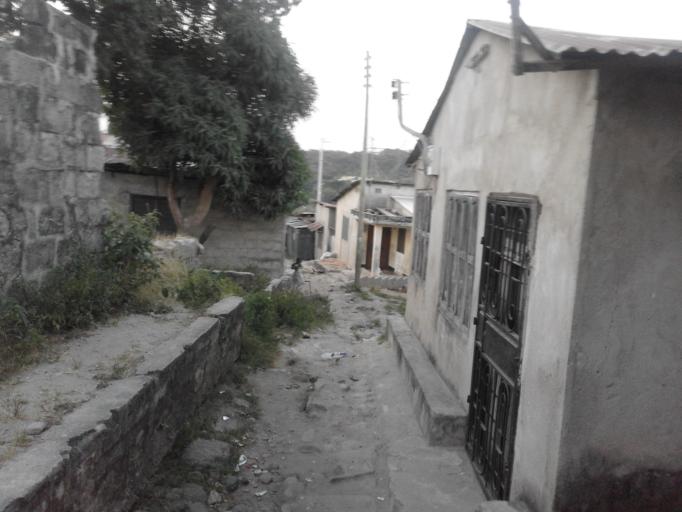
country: TZ
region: Dar es Salaam
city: Magomeni
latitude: -6.7863
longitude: 39.1999
